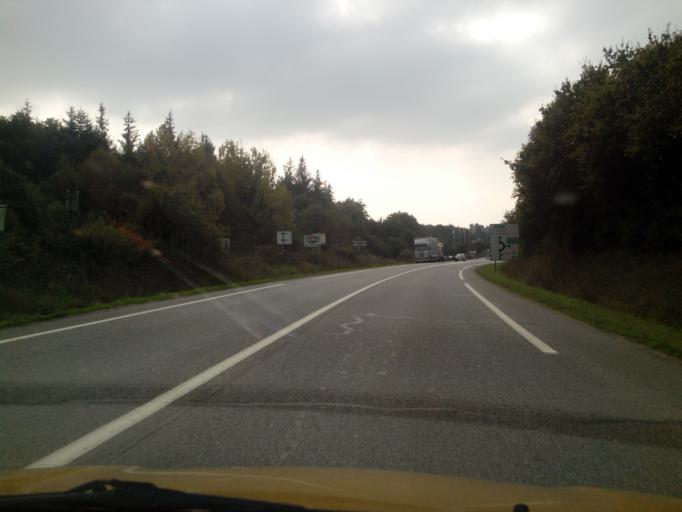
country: FR
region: Brittany
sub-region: Departement du Morbihan
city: Ploermel
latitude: 47.9219
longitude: -2.3862
